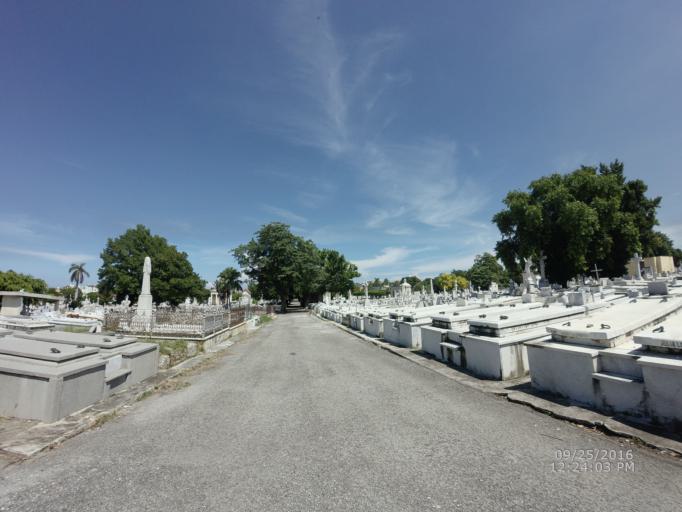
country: CU
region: La Habana
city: Havana
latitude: 23.1234
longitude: -82.3974
